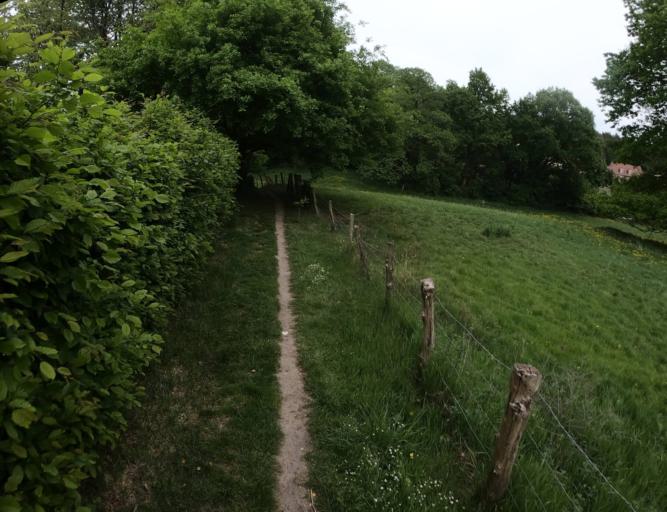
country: BE
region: Flanders
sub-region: Provincie Vlaams-Brabant
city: Beersel
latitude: 50.7402
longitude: 4.3181
